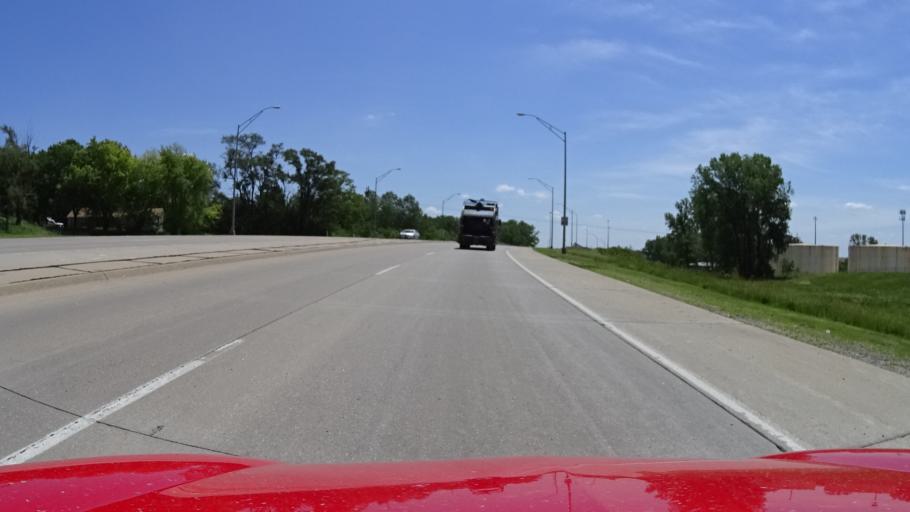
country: US
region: Nebraska
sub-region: Sarpy County
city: Offutt Air Force Base
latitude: 41.1174
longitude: -95.9321
